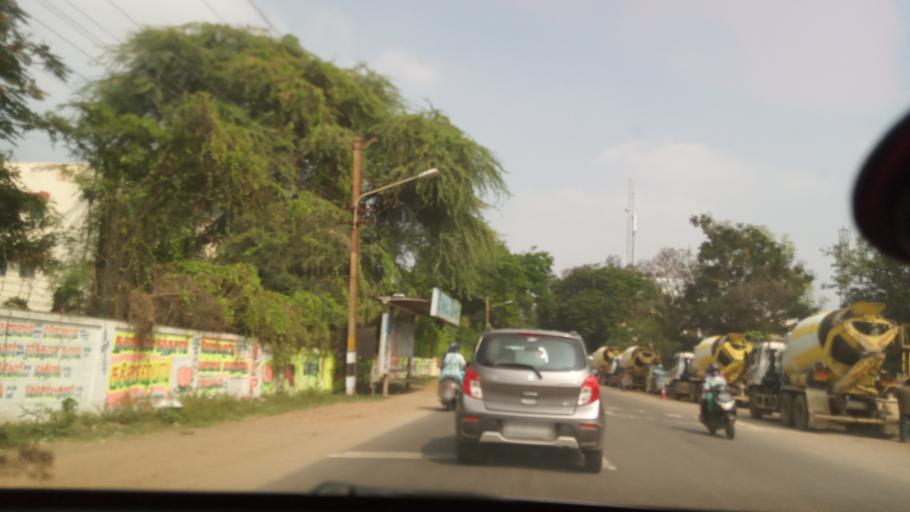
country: IN
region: Tamil Nadu
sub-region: Coimbatore
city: Coimbatore
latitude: 11.0145
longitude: 76.9441
